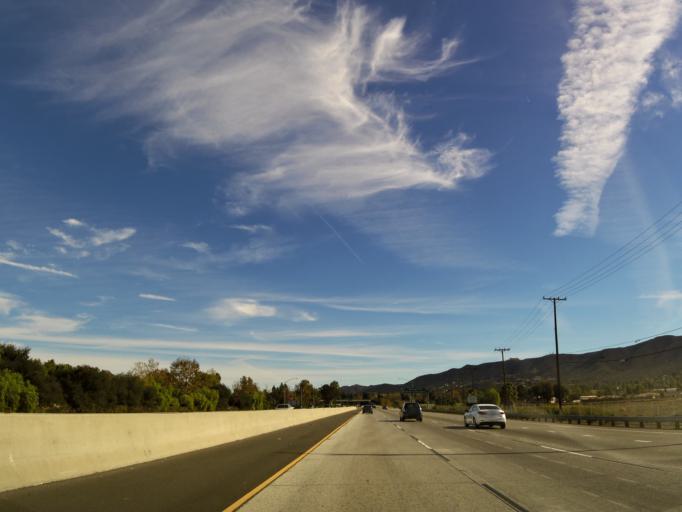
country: US
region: California
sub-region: Ventura County
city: Casa Conejo
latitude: 34.1869
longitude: -118.9329
